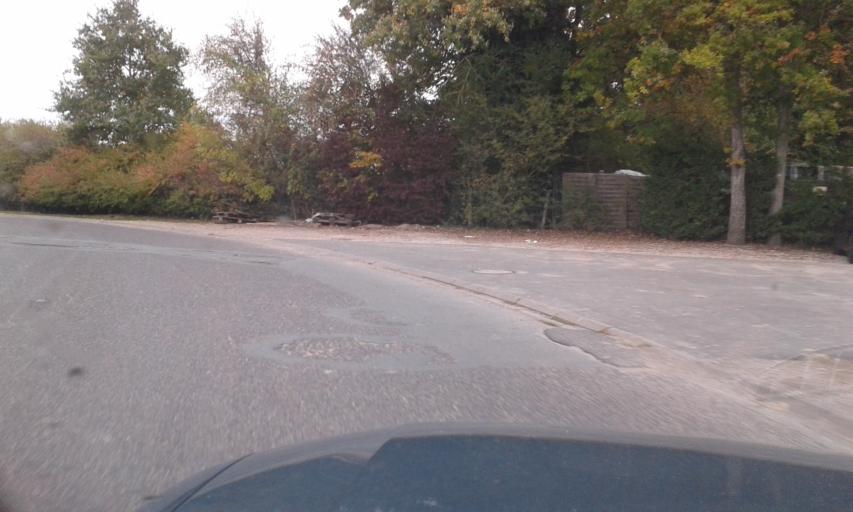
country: FR
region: Centre
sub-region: Departement du Loiret
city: Saran
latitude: 47.9636
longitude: 1.8841
